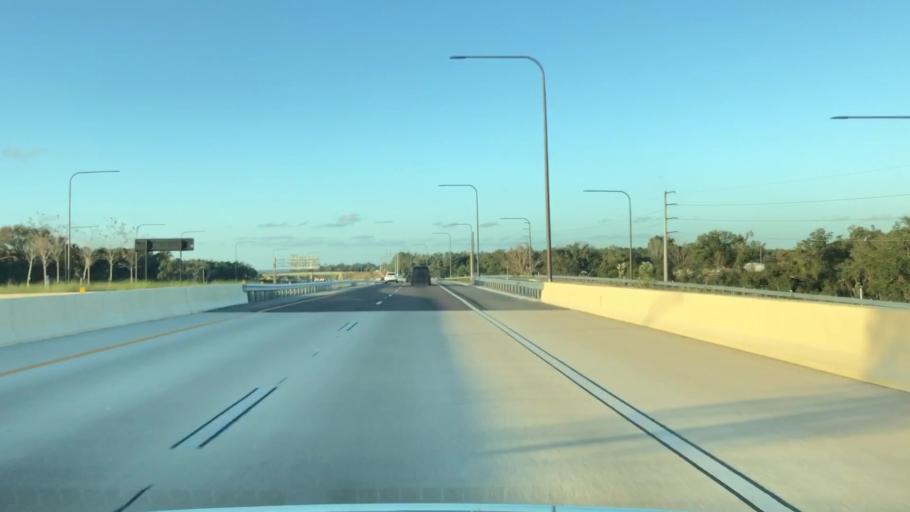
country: US
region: Florida
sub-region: Orange County
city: Zellwood
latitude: 28.7001
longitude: -81.5591
